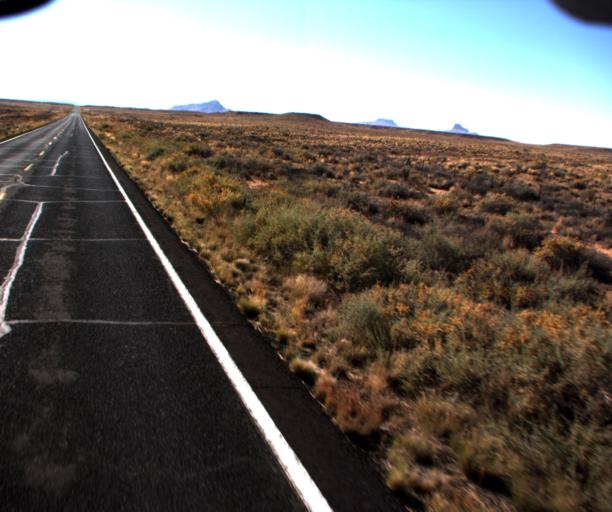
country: US
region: Arizona
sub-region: Navajo County
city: Dilkon
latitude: 35.5705
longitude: -110.4601
